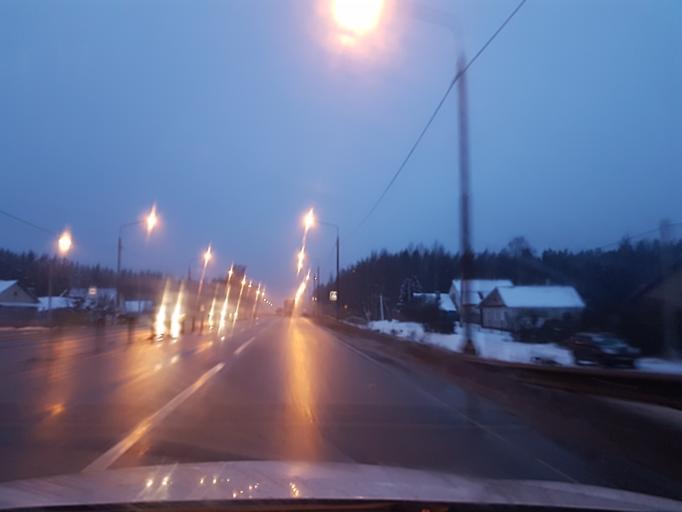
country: RU
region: Moskovskaya
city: Klin
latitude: 56.3972
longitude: 36.6567
